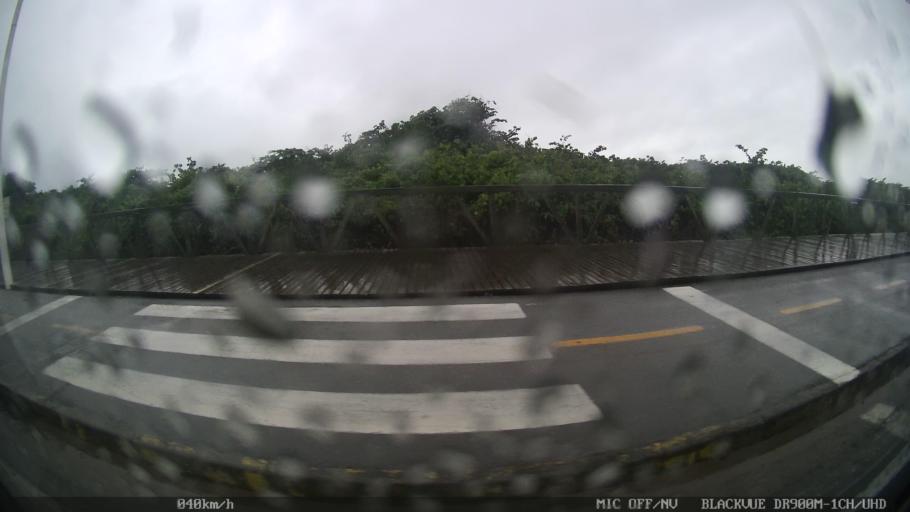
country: BR
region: Santa Catarina
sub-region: Navegantes
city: Navegantes
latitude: -26.8822
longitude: -48.6412
